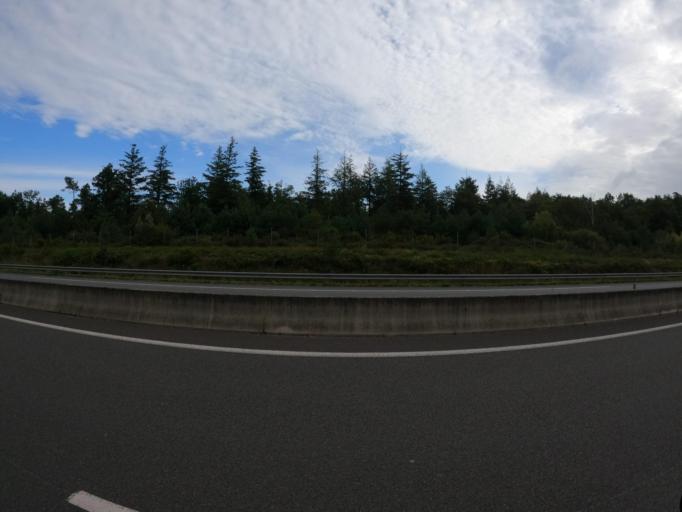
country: FR
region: Centre
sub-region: Departement d'Indre-et-Loire
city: Langeais
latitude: 47.3443
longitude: 0.4130
